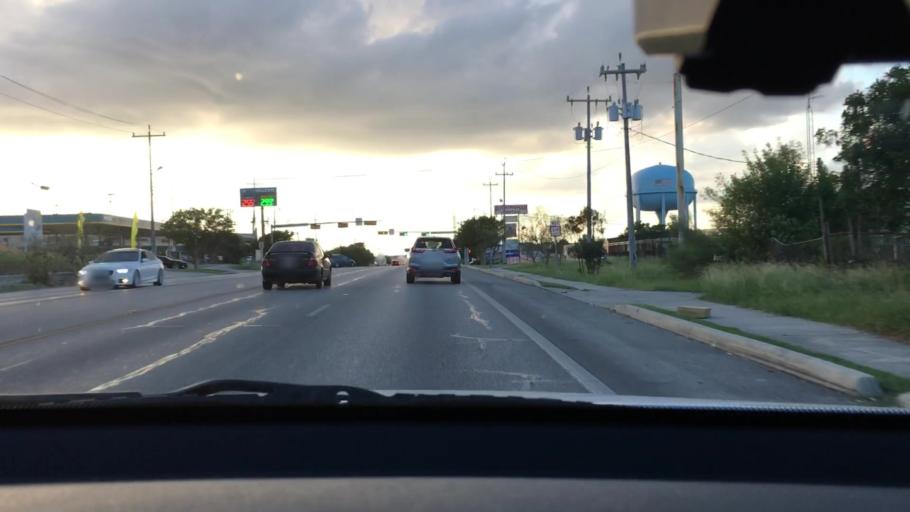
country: US
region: Texas
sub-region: Bexar County
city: Live Oak
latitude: 29.5578
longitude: -98.3205
